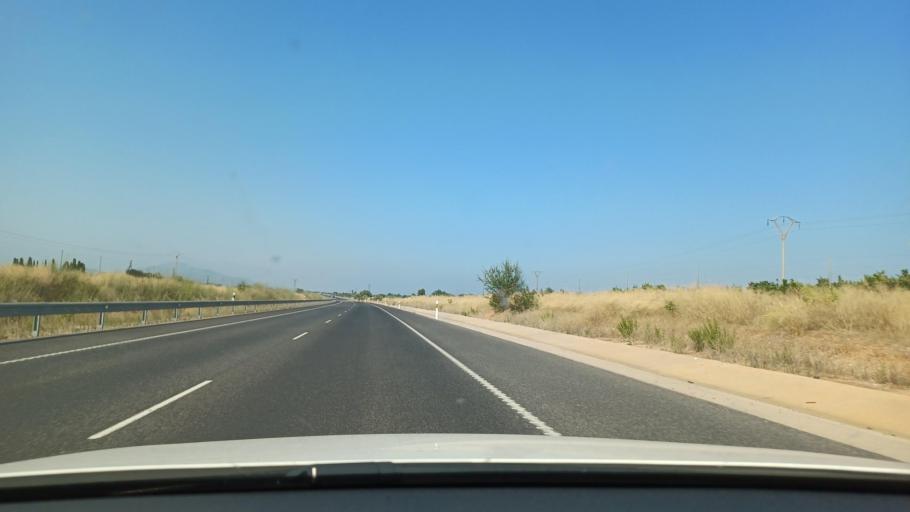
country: ES
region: Valencia
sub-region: Provincia de Castello
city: Benicarlo
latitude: 40.4502
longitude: 0.4250
